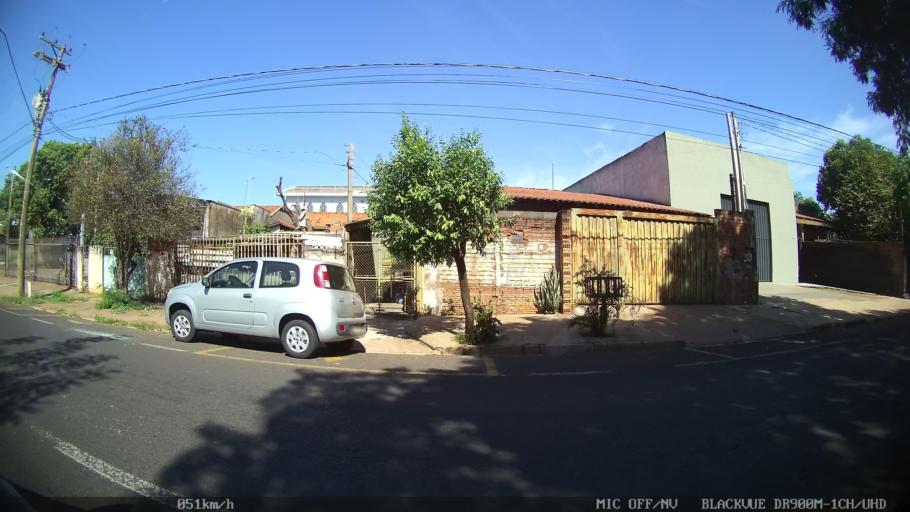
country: BR
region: Sao Paulo
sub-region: Sao Jose Do Rio Preto
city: Sao Jose do Rio Preto
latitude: -20.7782
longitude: -49.3941
